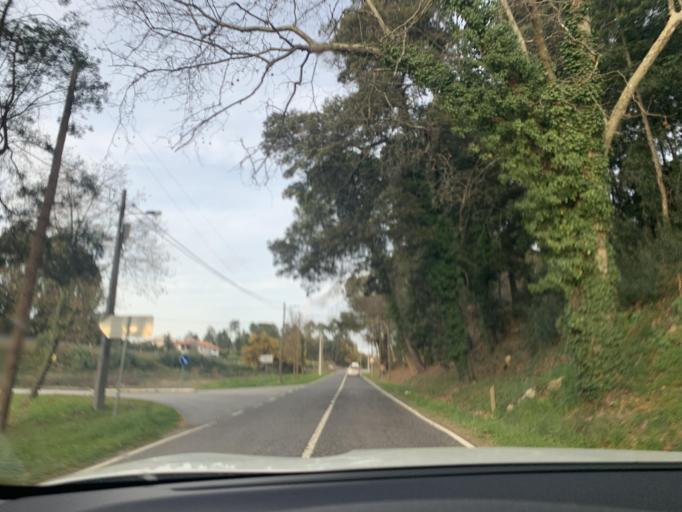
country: PT
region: Viseu
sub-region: Concelho de Tondela
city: Tondela
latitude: 40.5922
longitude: -8.0074
